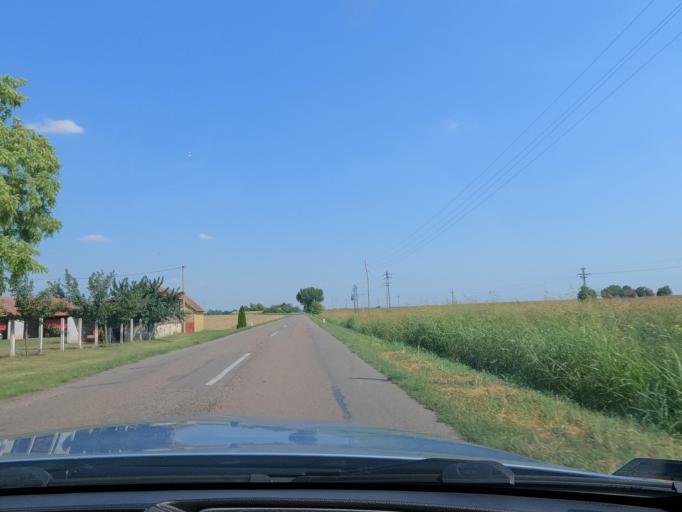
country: RS
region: Autonomna Pokrajina Vojvodina
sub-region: Severnobacki Okrug
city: Mali Igos
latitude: 45.7531
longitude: 19.7838
